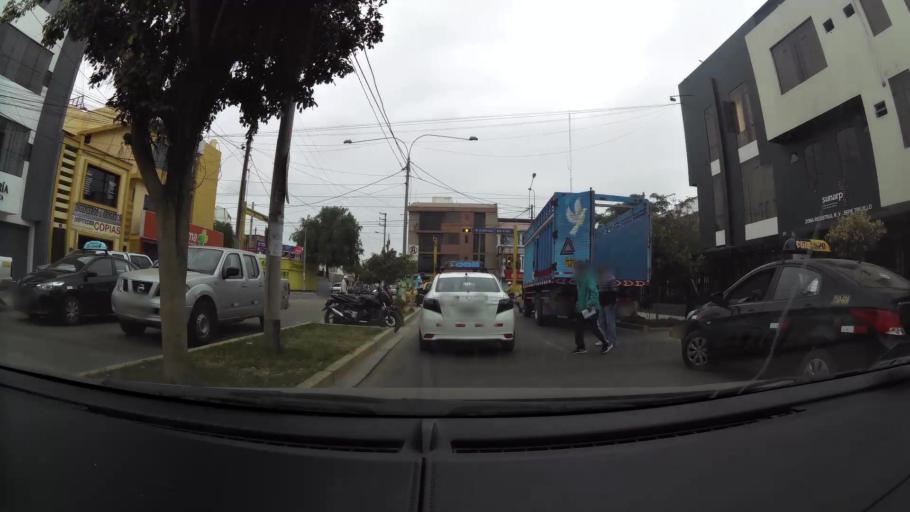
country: PE
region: La Libertad
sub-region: Provincia de Trujillo
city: Buenos Aires
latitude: -8.1254
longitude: -79.0400
